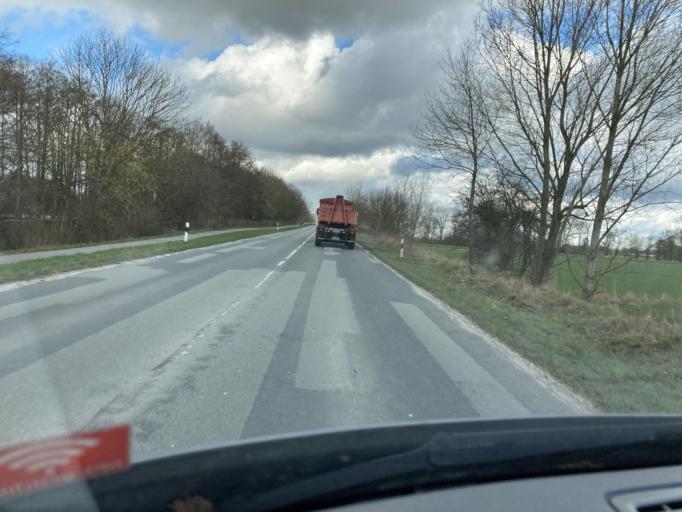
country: DE
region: Lower Saxony
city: Sande
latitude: 53.5088
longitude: 8.0234
